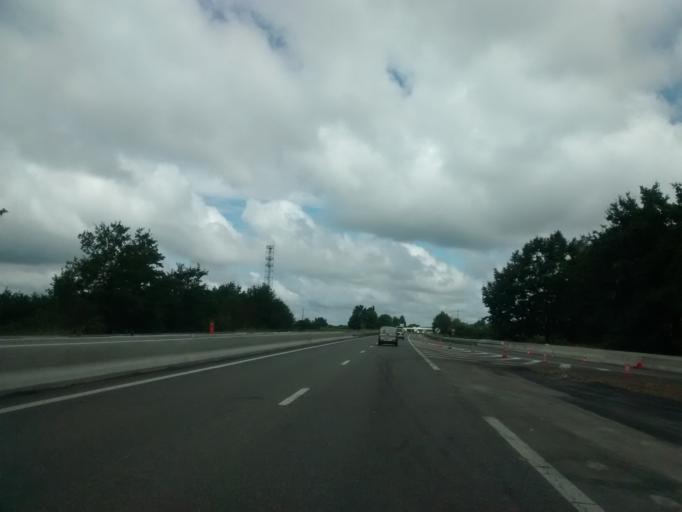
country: FR
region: Aquitaine
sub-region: Departement des Pyrenees-Atlantiques
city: Artix
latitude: 43.3962
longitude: -0.5476
